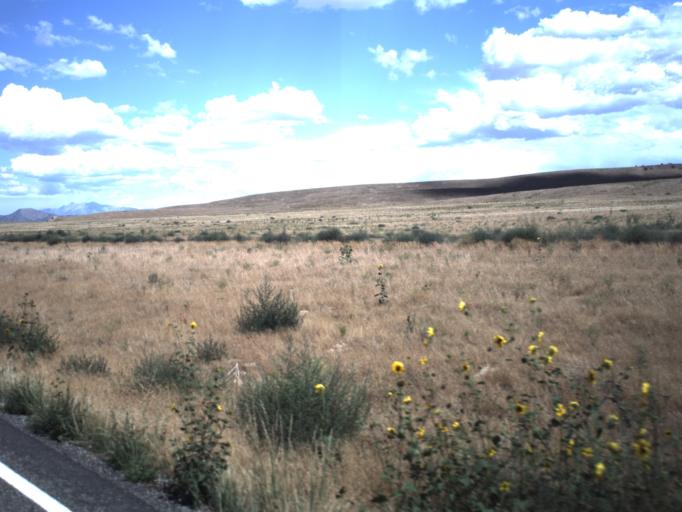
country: US
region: Utah
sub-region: Millard County
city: Delta
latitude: 39.6611
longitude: -112.2799
